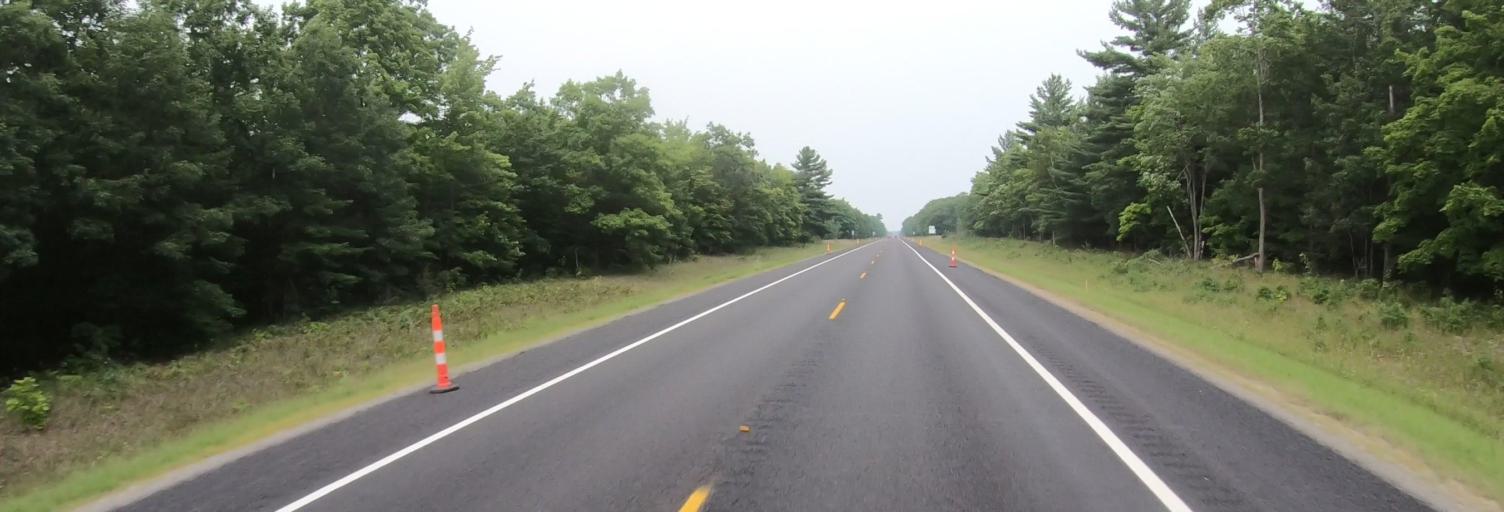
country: US
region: Michigan
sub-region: Mackinac County
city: Saint Ignace
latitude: 45.7073
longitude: -84.7649
